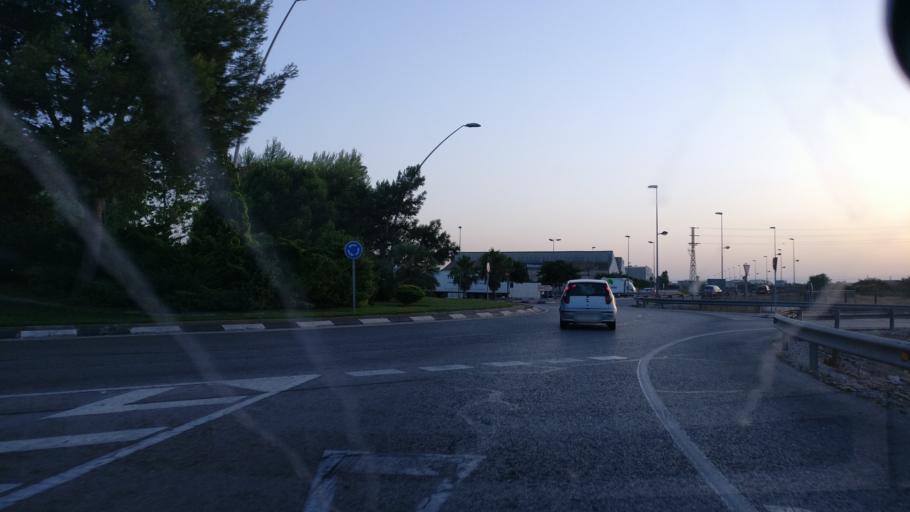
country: ES
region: Valencia
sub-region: Provincia de Valencia
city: Xirivella
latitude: 39.4647
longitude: -0.4396
